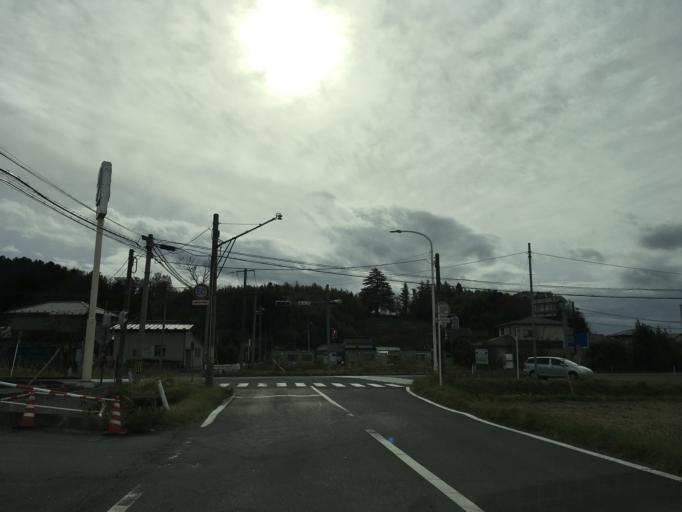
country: JP
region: Iwate
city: Ichinoseki
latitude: 38.7323
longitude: 141.2748
